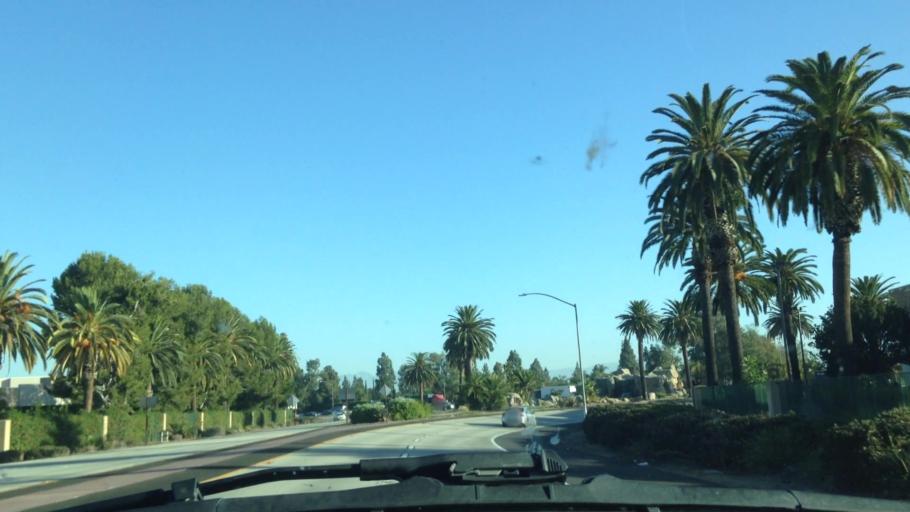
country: US
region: California
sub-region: Los Angeles County
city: Cerritos
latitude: 33.8687
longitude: -118.0570
